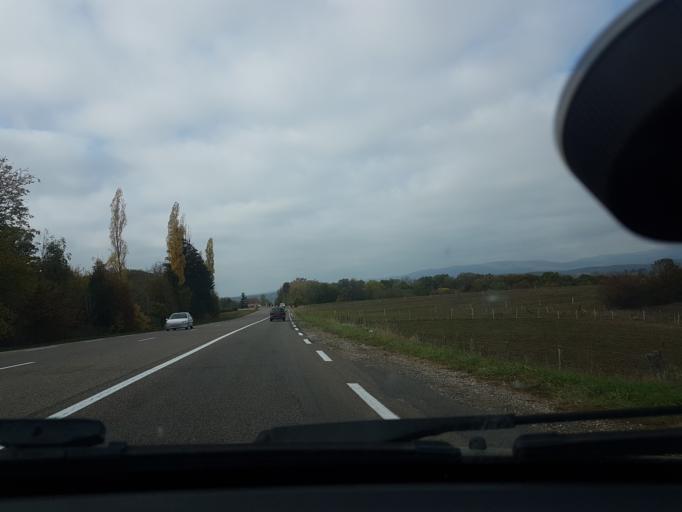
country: FR
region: Franche-Comte
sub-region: Departement de la Haute-Saone
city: Chalonvillars
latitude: 47.6477
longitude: 6.7710
